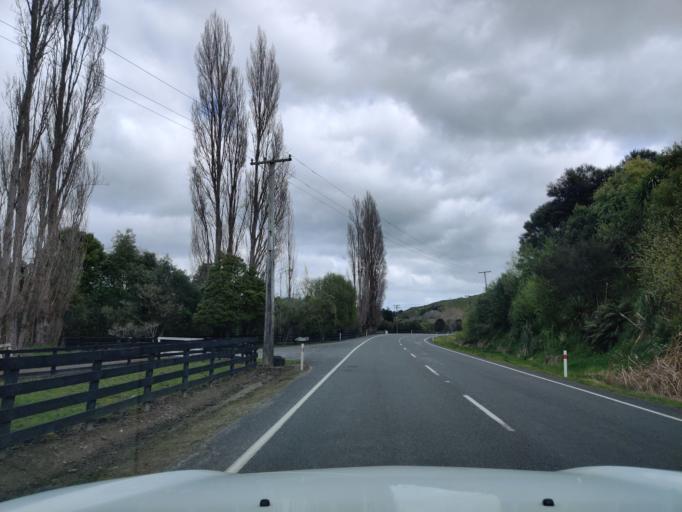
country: NZ
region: Manawatu-Wanganui
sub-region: Wanganui District
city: Wanganui
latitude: -39.8445
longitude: 175.1506
